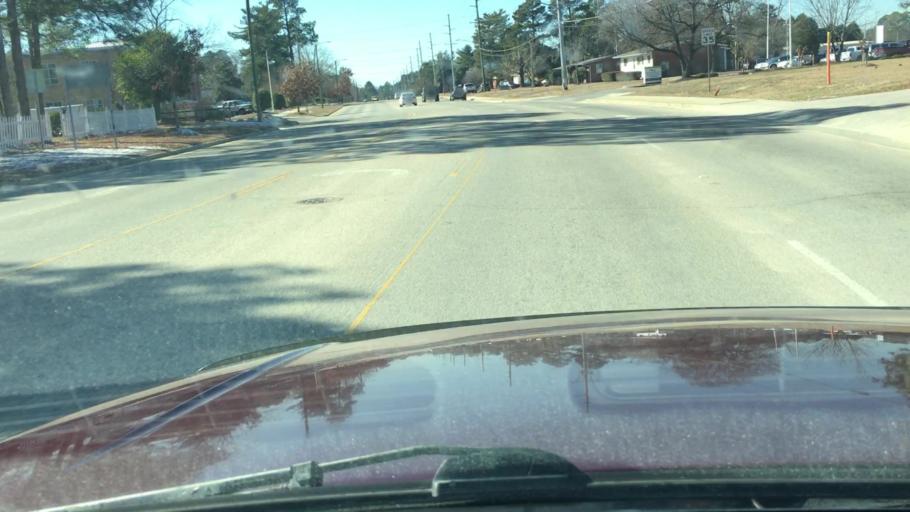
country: US
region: North Carolina
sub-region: Cumberland County
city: Hope Mills
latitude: 35.0297
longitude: -78.9343
